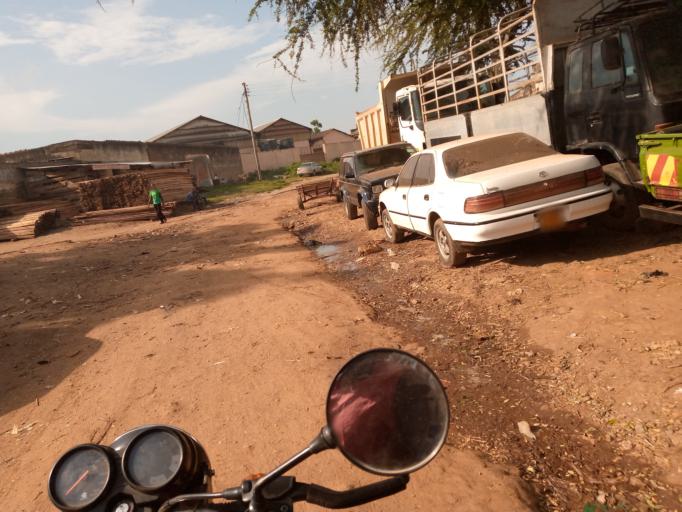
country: UG
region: Eastern Region
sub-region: Mbale District
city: Mbale
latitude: 1.0779
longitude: 34.1619
